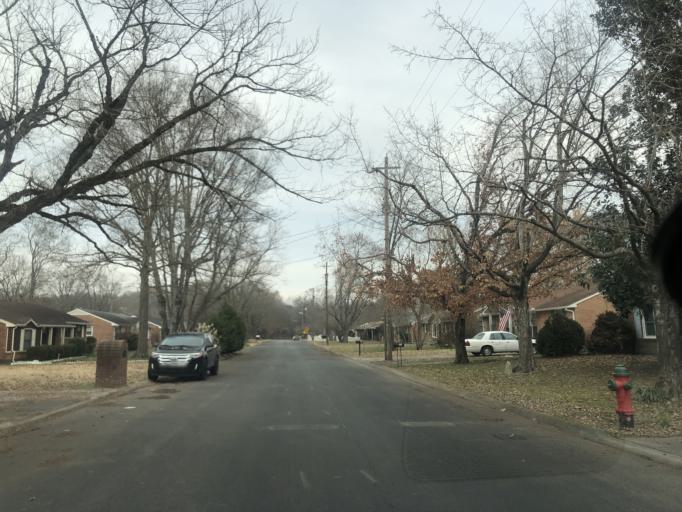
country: US
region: Tennessee
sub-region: Davidson County
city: Oak Hill
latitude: 36.0909
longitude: -86.7200
